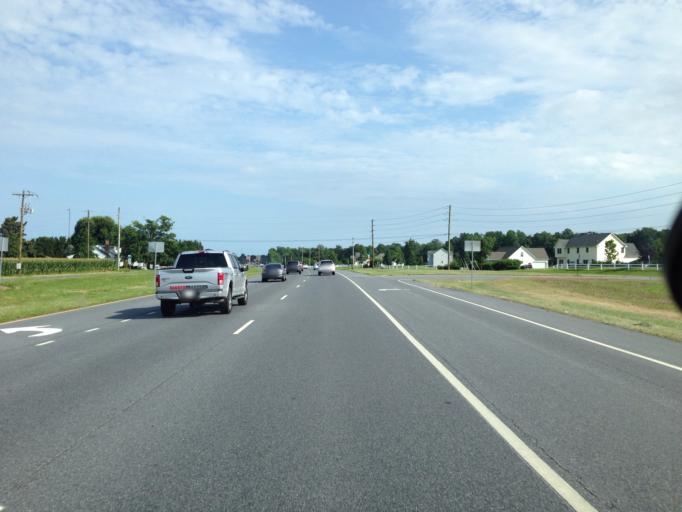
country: US
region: Delaware
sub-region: Sussex County
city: Milton
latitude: 38.8299
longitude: -75.3132
